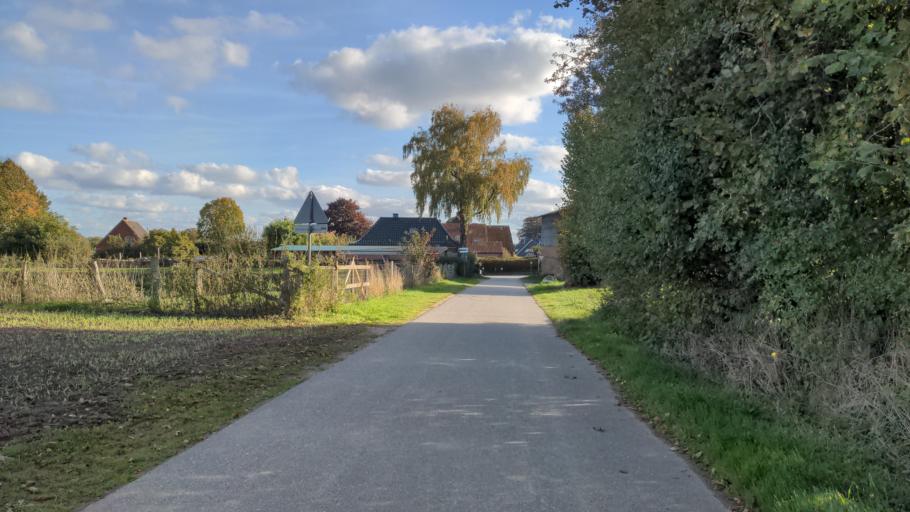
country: DE
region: Schleswig-Holstein
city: Schashagen
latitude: 54.1335
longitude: 10.9081
